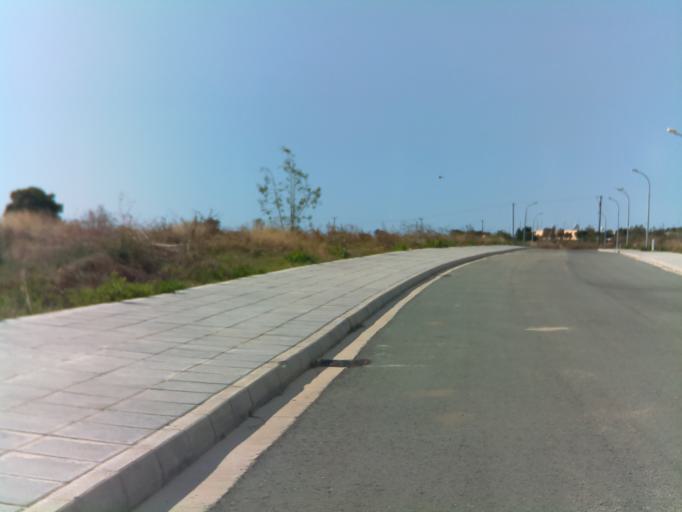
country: CY
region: Limassol
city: Pissouri
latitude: 34.6492
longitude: 32.6997
